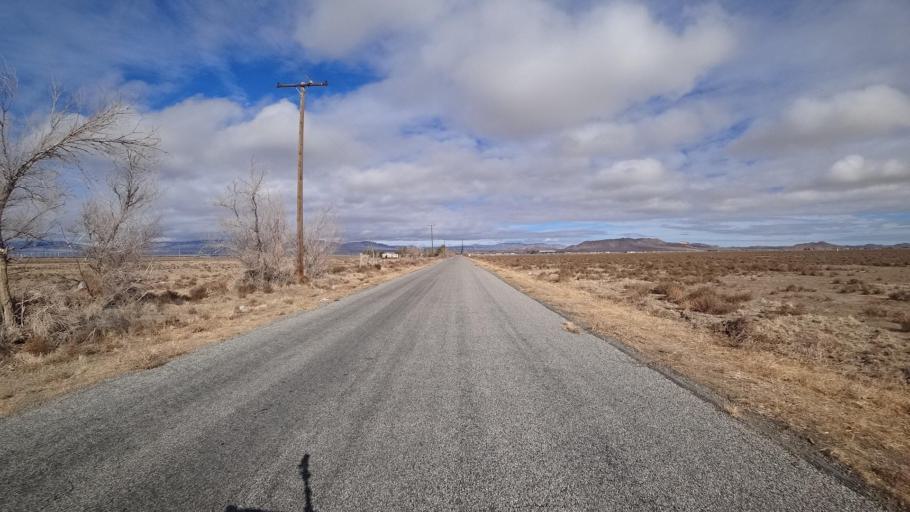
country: US
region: California
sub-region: Kern County
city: Rosamond
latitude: 34.8283
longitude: -118.3082
